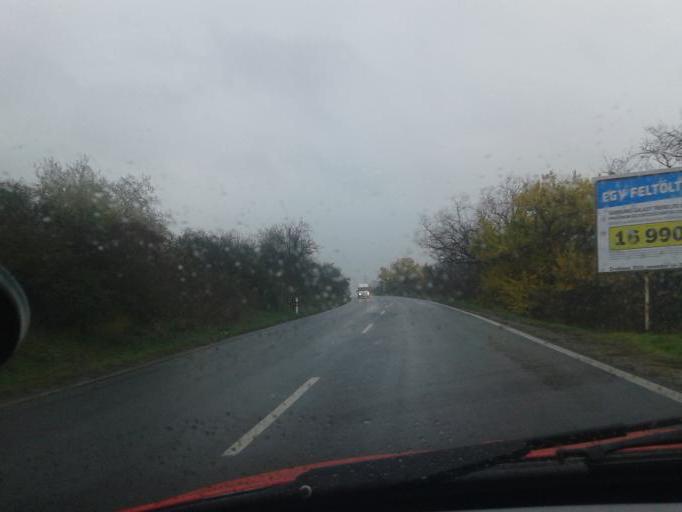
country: HU
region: Pest
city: Diosd
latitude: 47.4153
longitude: 18.9701
